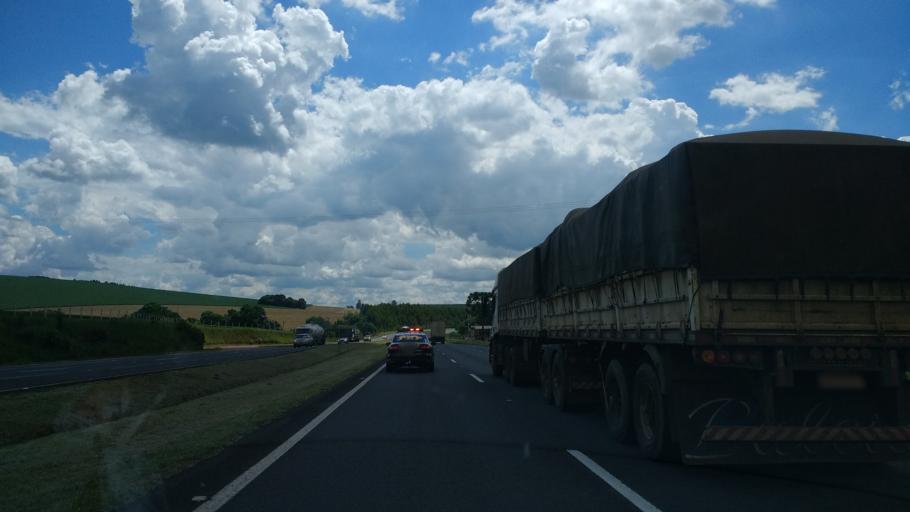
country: BR
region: Parana
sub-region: Palmeira
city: Palmeira
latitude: -25.2612
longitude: -50.0047
